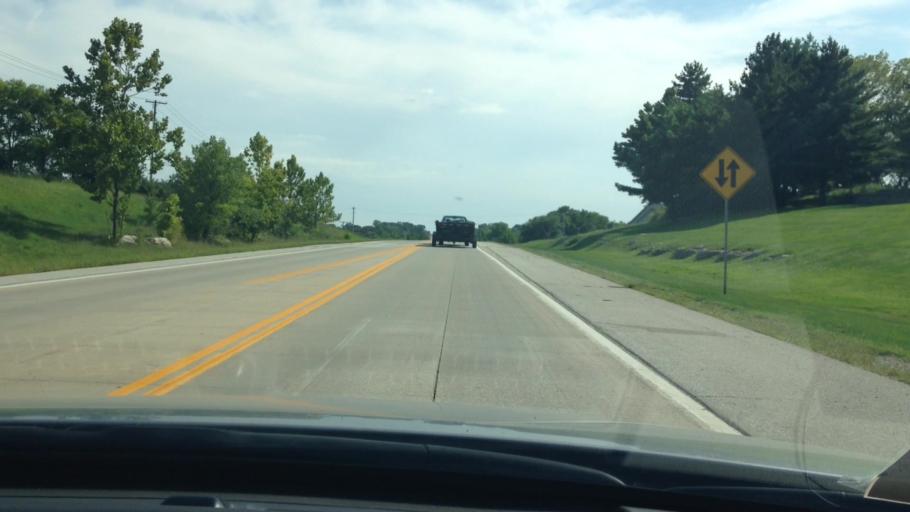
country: US
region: Missouri
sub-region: Cass County
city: Belton
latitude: 38.8261
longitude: -94.5852
